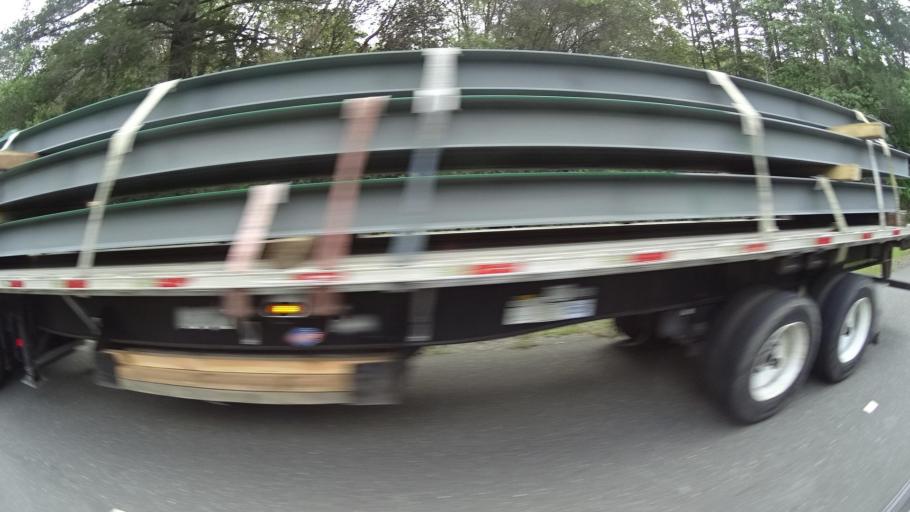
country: US
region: California
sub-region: Humboldt County
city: Redway
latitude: 40.1963
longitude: -123.5919
